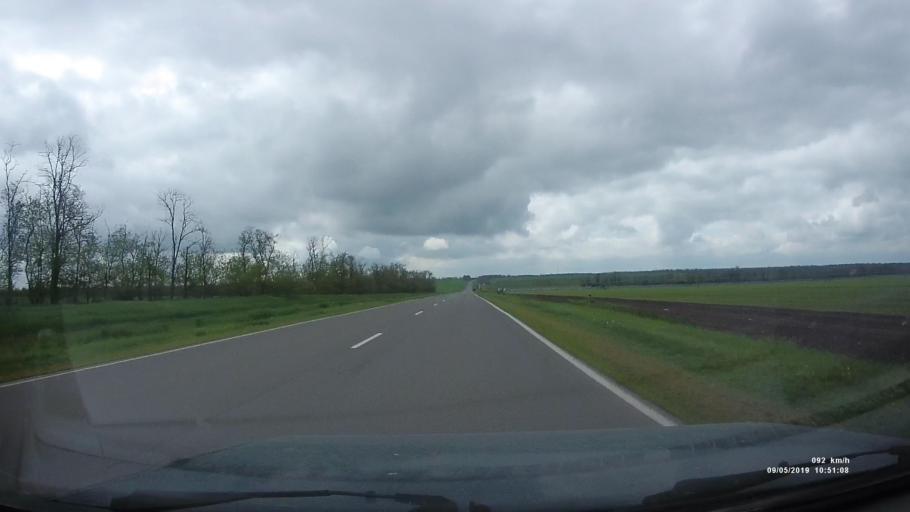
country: RU
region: Rostov
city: Peshkovo
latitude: 46.9189
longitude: 39.3552
